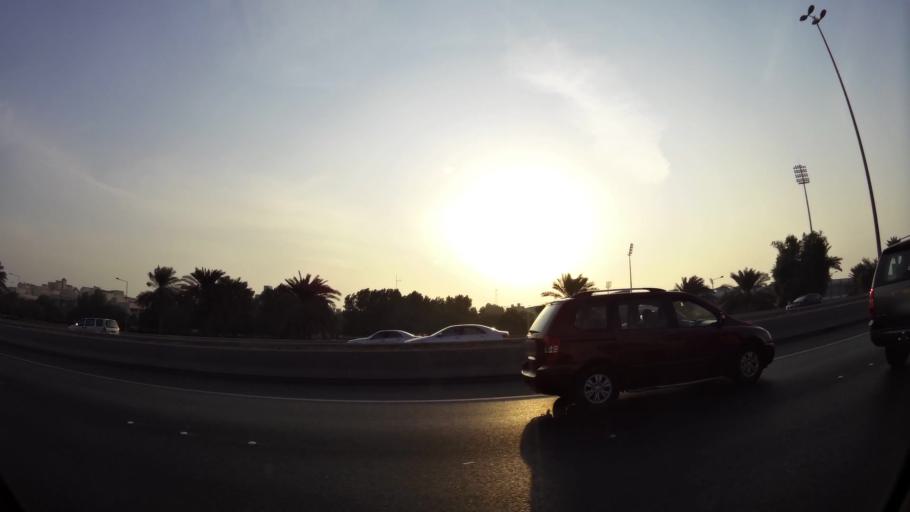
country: KW
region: Muhafazat Hawalli
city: Salwa
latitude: 29.2911
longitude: 48.0714
